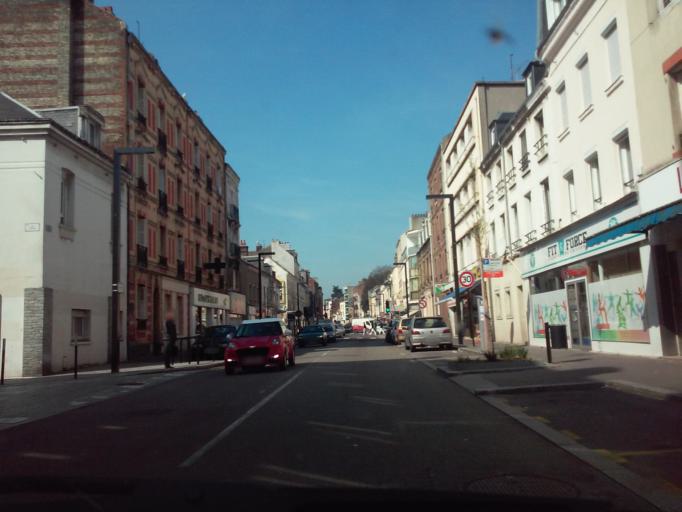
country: FR
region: Haute-Normandie
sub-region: Departement de la Seine-Maritime
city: Le Havre
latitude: 49.4999
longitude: 0.1279
